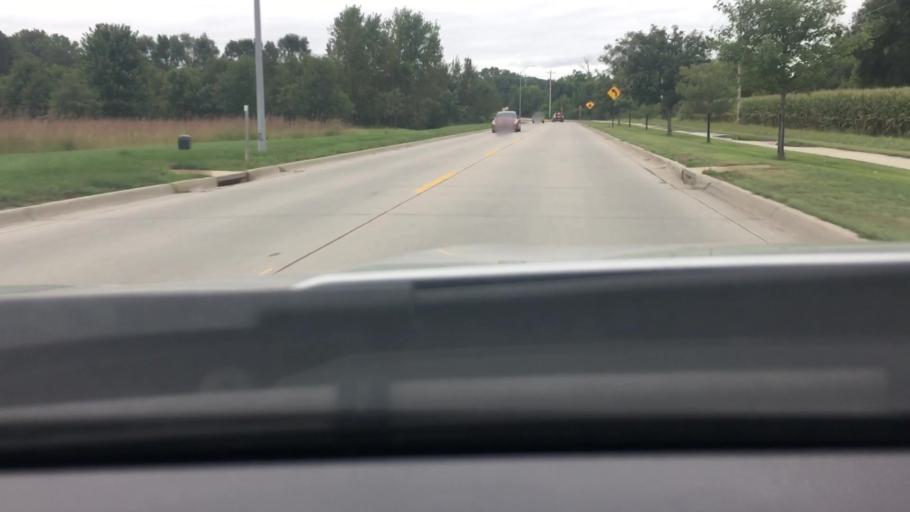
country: US
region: Iowa
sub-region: Pottawattamie County
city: Council Bluffs
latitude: 41.2631
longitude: -95.8045
